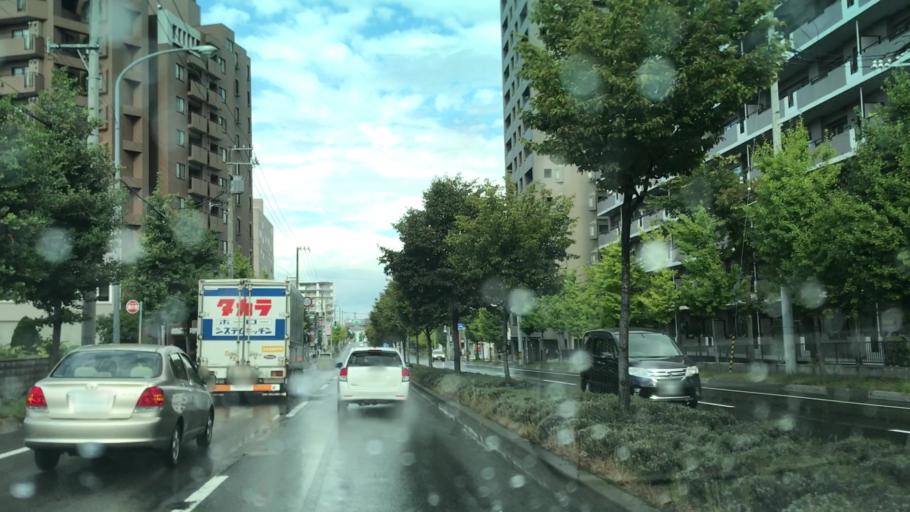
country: JP
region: Hokkaido
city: Sapporo
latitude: 43.0870
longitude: 141.2814
